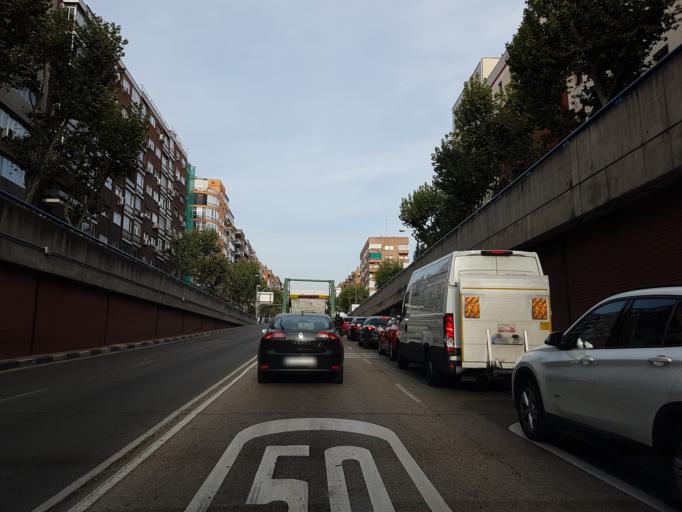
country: ES
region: Madrid
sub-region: Provincia de Madrid
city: Retiro
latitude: 40.4069
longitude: -3.6711
